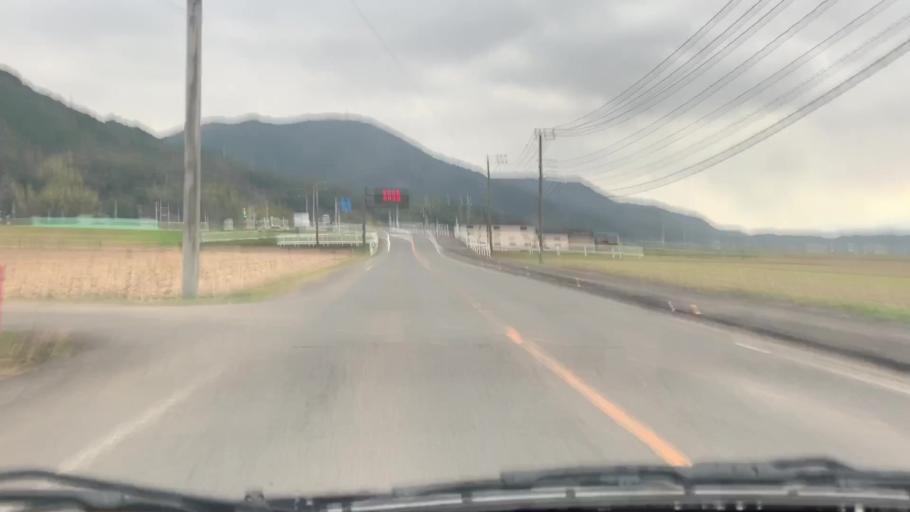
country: JP
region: Saga Prefecture
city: Takeocho-takeo
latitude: 33.2034
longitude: 130.0509
